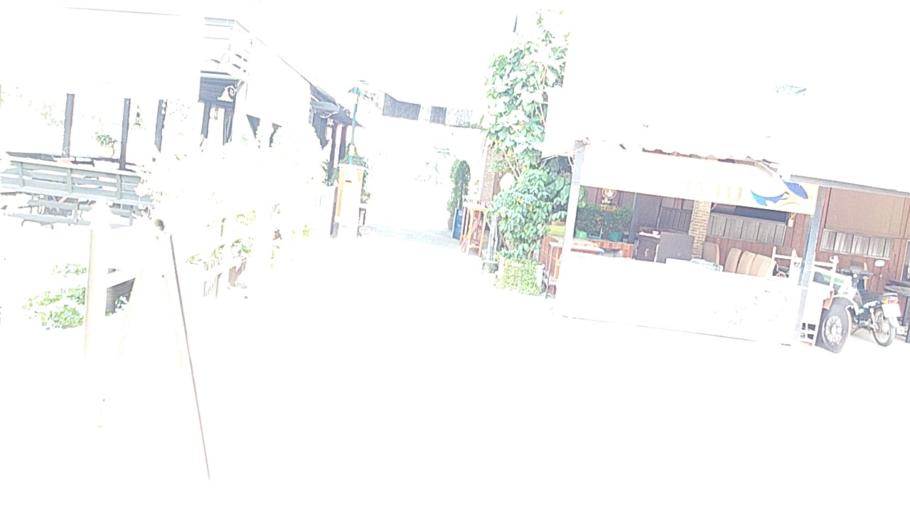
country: TH
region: Nonthaburi
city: Sai Noi
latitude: 13.9782
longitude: 100.3122
